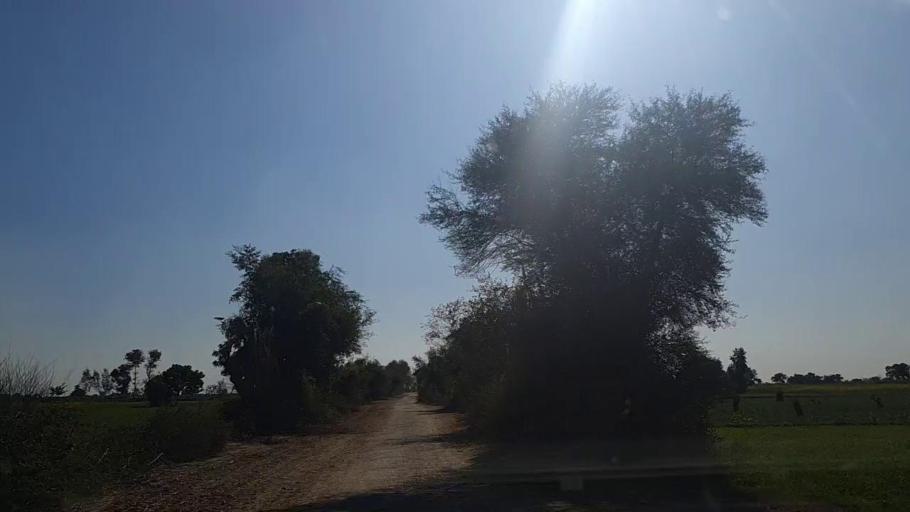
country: PK
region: Sindh
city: Sakrand
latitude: 26.2430
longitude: 68.1999
